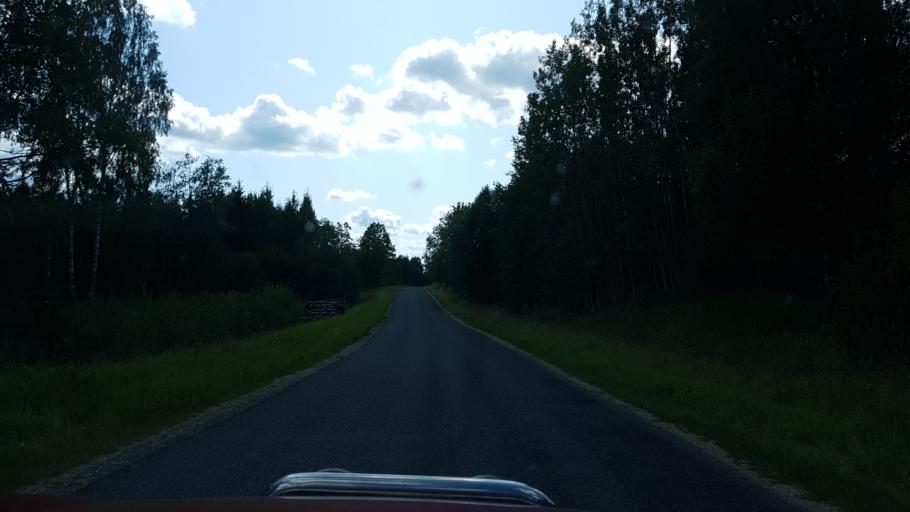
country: LV
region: Aluksnes Rajons
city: Aluksne
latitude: 57.5994
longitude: 27.0912
